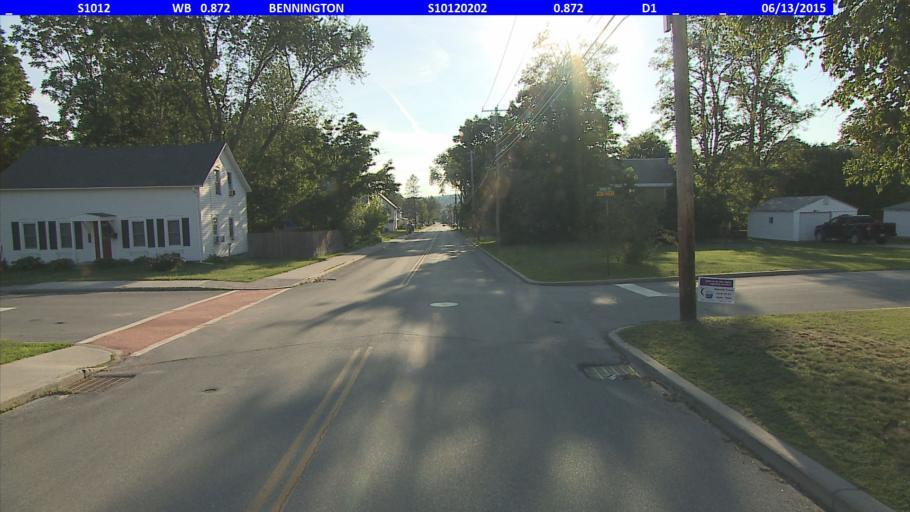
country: US
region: Vermont
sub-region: Bennington County
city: Bennington
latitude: 42.8839
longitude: -73.1856
